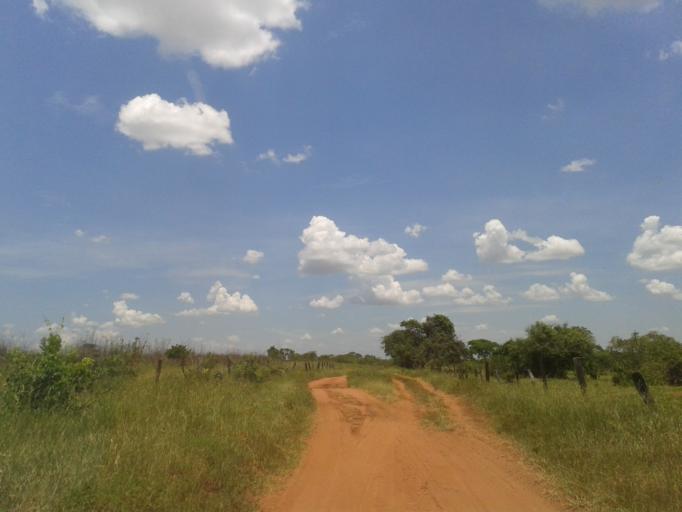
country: BR
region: Minas Gerais
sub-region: Santa Vitoria
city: Santa Vitoria
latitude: -19.2260
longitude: -50.4527
